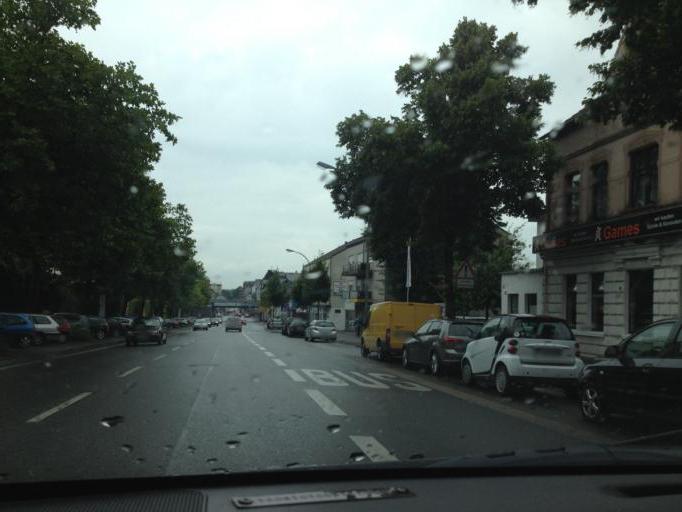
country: DE
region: North Rhine-Westphalia
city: Schwerte
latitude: 51.4881
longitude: 7.5546
